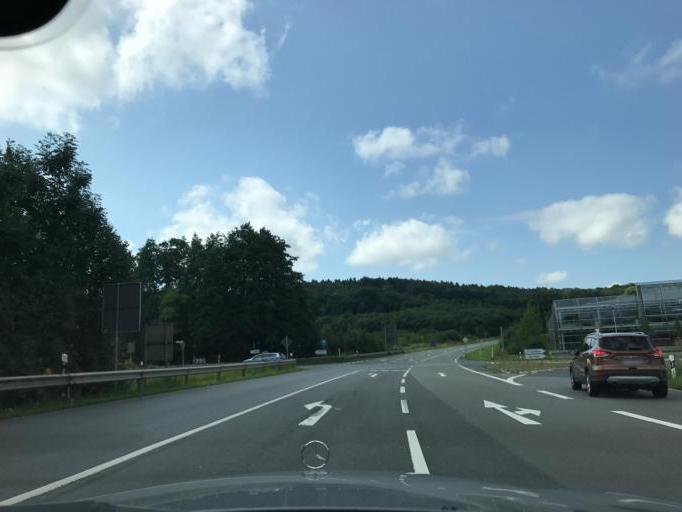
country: DE
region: North Rhine-Westphalia
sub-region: Regierungsbezirk Munster
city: Lotte
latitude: 52.2646
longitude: 7.8944
